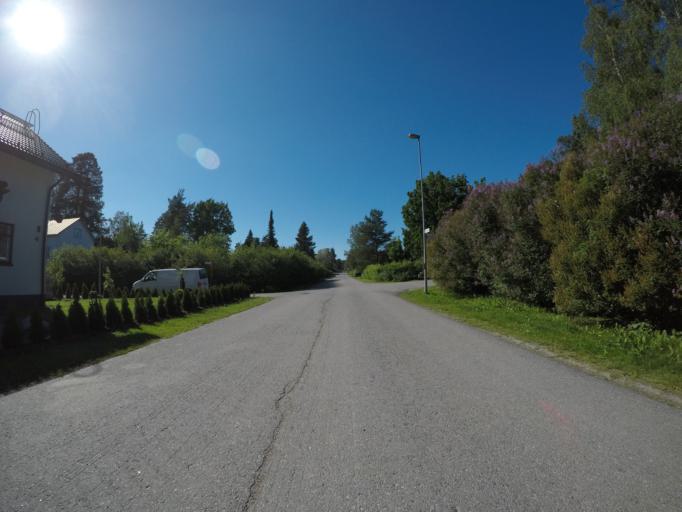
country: FI
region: Haeme
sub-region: Haemeenlinna
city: Haemeenlinna
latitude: 61.0103
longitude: 24.4851
